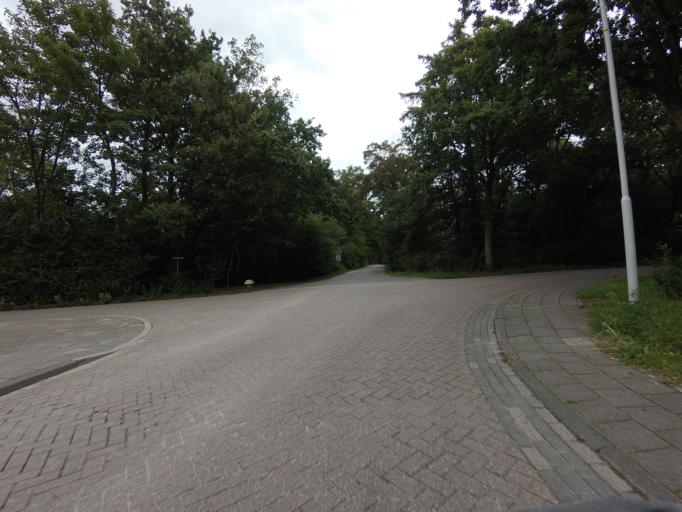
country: NL
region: Friesland
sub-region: Gemeente Terschelling
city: West-Terschelling
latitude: 53.3686
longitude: 5.2166
